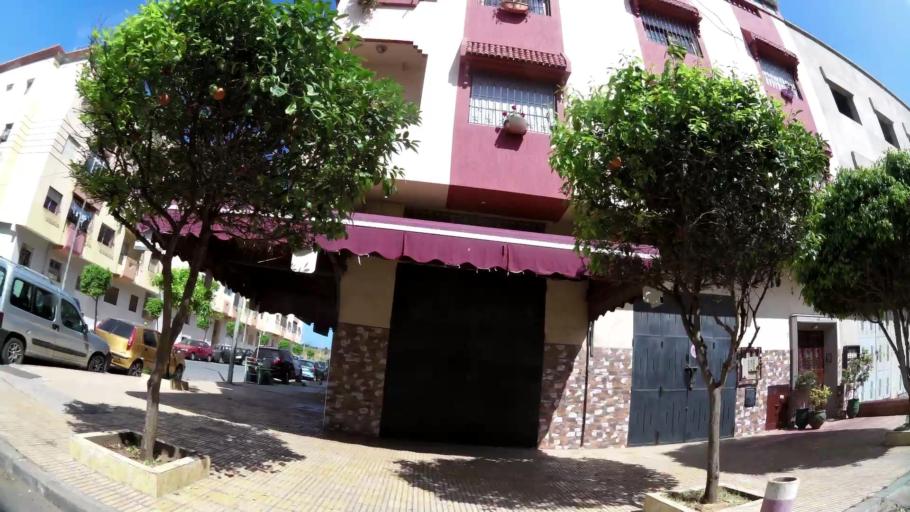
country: MA
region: Rabat-Sale-Zemmour-Zaer
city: Sale
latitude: 34.0780
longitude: -6.7911
